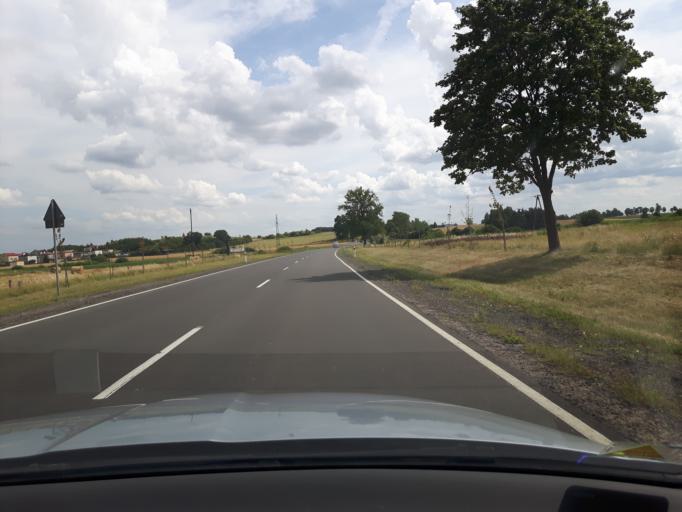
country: PL
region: Warmian-Masurian Voivodeship
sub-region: Powiat nidzicki
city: Nidzica
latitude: 53.3684
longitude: 20.3953
